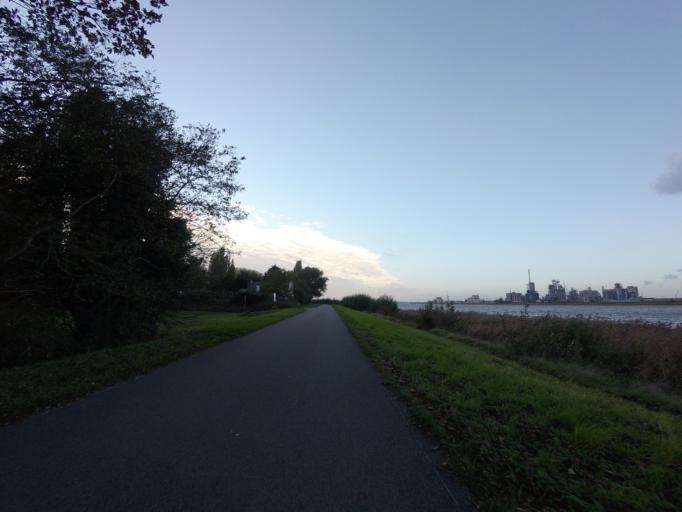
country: BE
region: Flanders
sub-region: Provincie Antwerpen
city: Antwerpen
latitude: 51.2364
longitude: 4.3820
